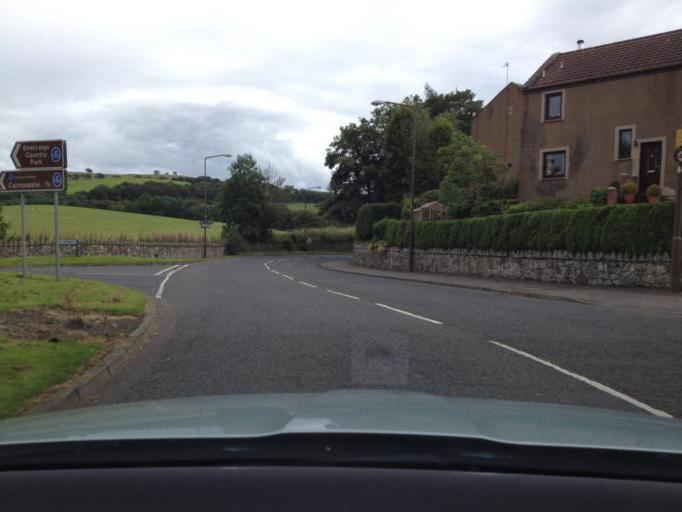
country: GB
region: Scotland
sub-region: West Lothian
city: Bathgate
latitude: 55.9318
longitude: -3.6488
